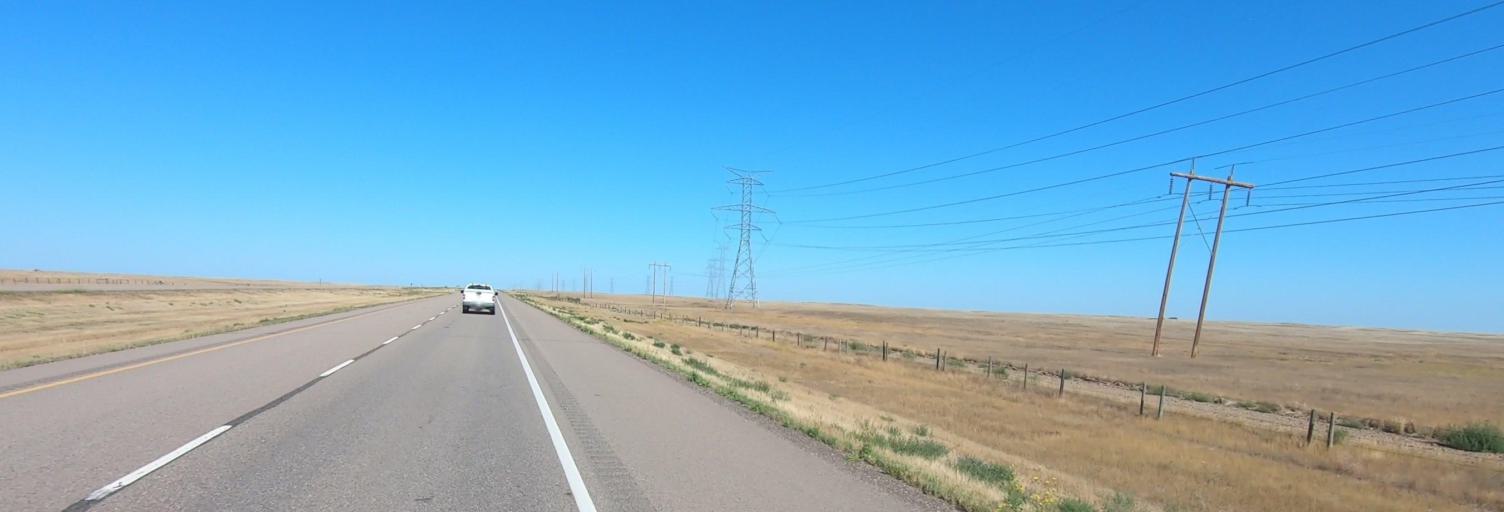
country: CA
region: Alberta
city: Bow Island
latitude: 50.2962
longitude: -111.3081
